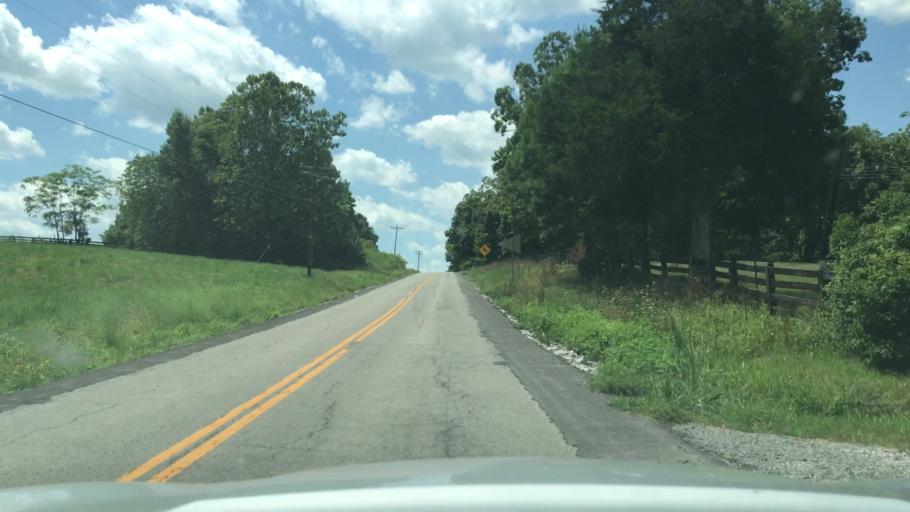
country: US
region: Kentucky
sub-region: Muhlenberg County
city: Greenville
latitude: 37.1280
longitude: -87.2979
